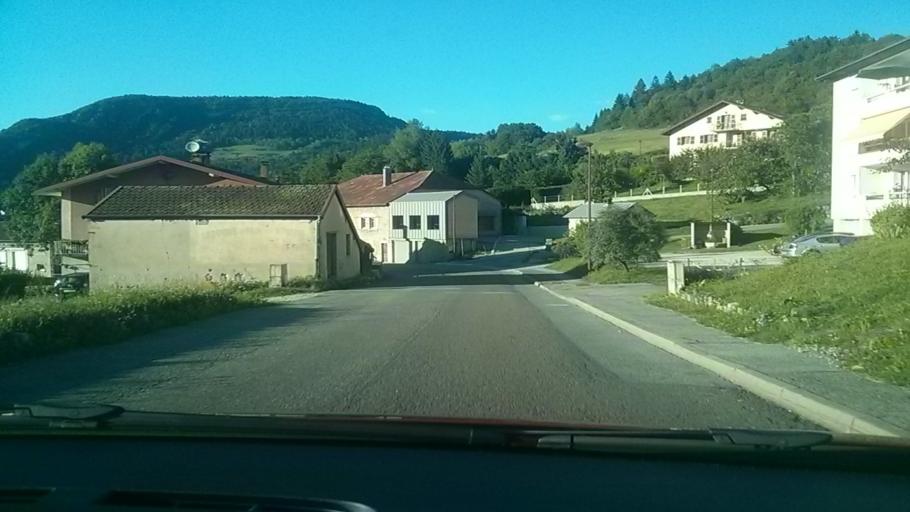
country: FR
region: Franche-Comte
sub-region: Departement du Jura
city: Saint-Claude
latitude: 46.3705
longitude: 5.8746
